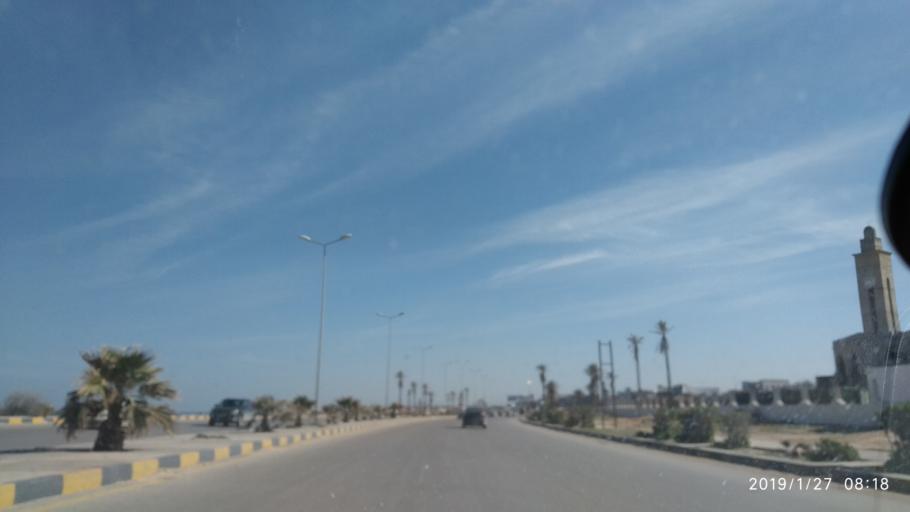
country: LY
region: Tripoli
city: Tagiura
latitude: 32.8951
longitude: 13.3375
